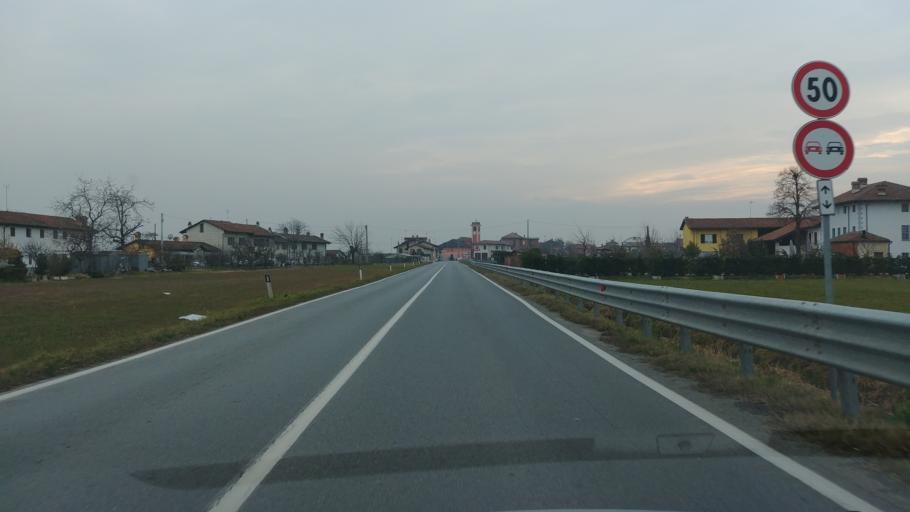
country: IT
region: Piedmont
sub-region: Provincia di Cuneo
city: Sant'Albano Stura
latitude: 44.5142
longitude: 7.6919
